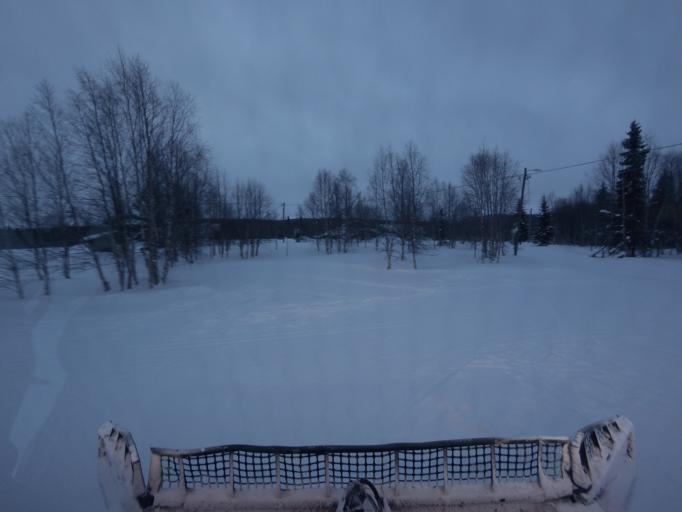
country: FI
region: Lapland
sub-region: Tunturi-Lappi
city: Kolari
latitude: 67.6177
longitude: 24.1618
